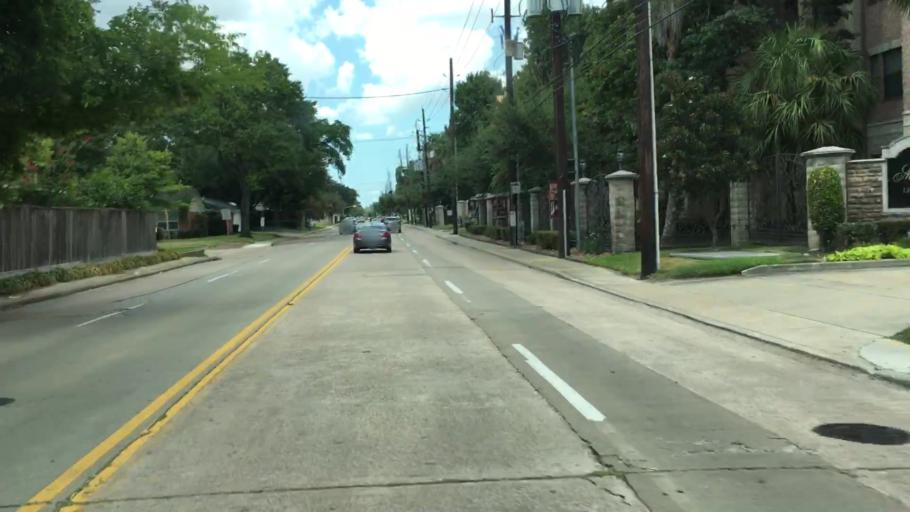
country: US
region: Texas
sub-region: Harris County
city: Bellaire
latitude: 29.7431
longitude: -95.4670
